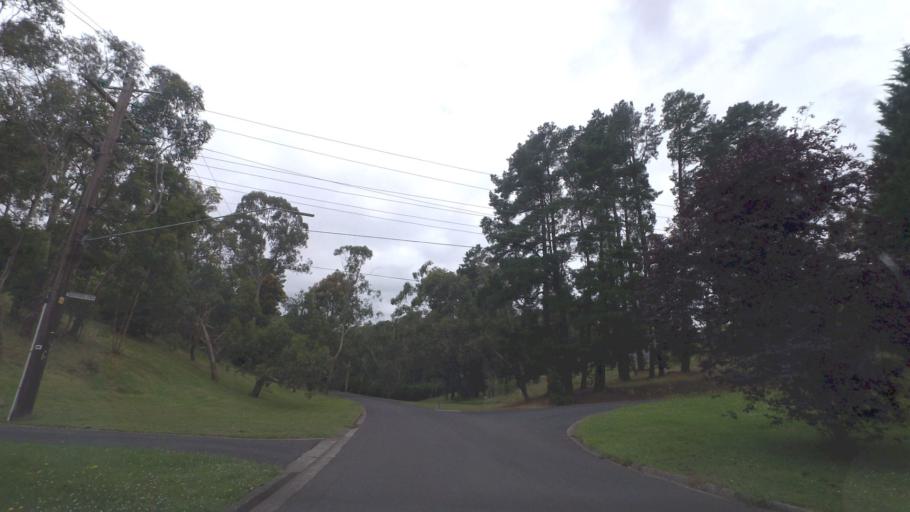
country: AU
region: Victoria
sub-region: Manningham
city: Park Orchards
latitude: -37.7850
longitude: 145.2185
